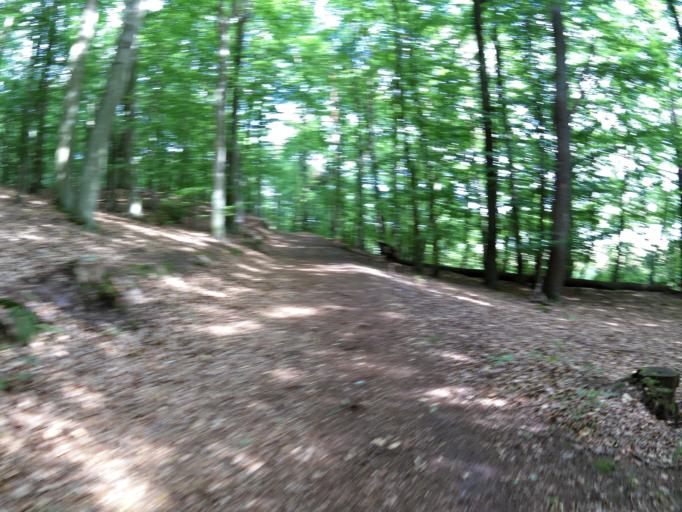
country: DE
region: Mecklenburg-Vorpommern
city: Seebad Bansin
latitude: 53.9529
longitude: 14.1083
